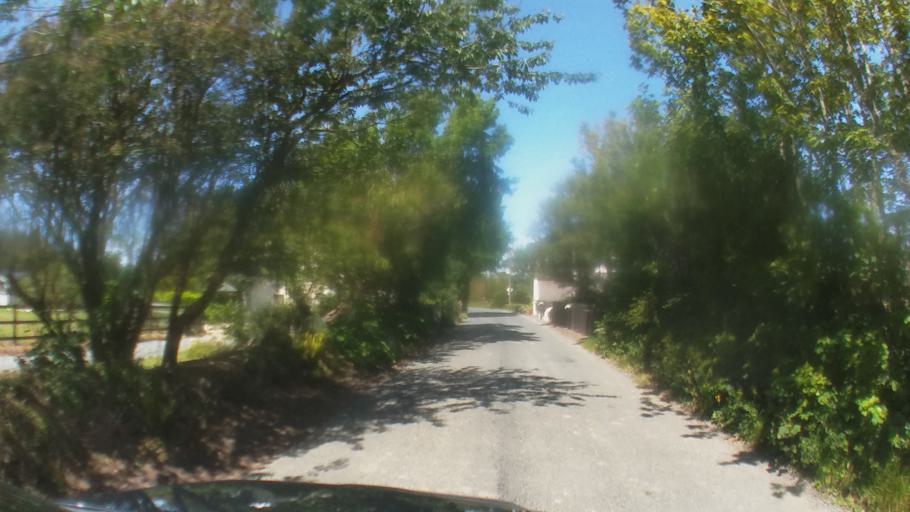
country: IE
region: Leinster
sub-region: Loch Garman
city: Loch Garman
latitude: 52.2337
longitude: -6.5657
